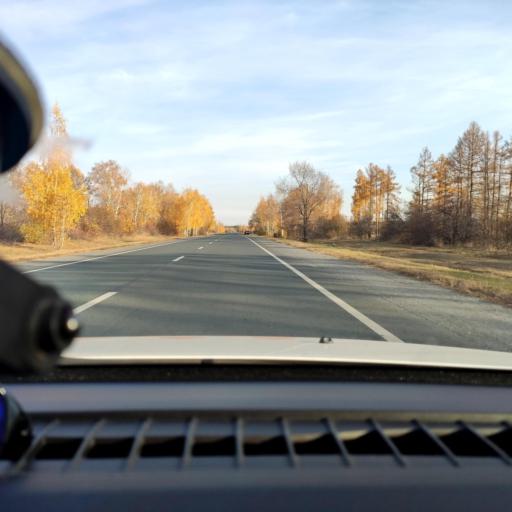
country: RU
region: Samara
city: Volzhskiy
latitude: 53.4587
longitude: 50.1269
